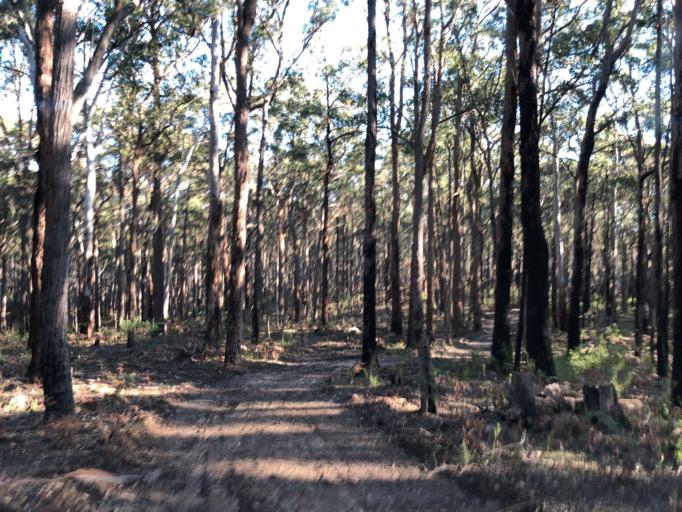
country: AU
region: Victoria
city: Brown Hill
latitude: -37.5094
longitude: 144.1830
